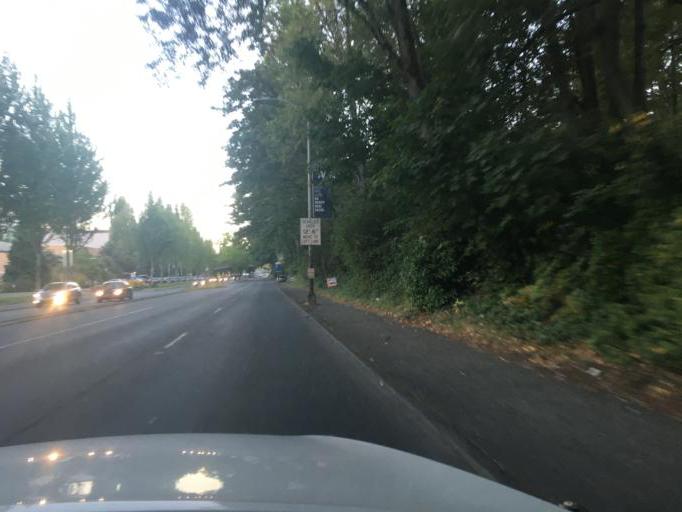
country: US
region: Washington
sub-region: King County
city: Seattle
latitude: 47.6549
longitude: -122.3025
